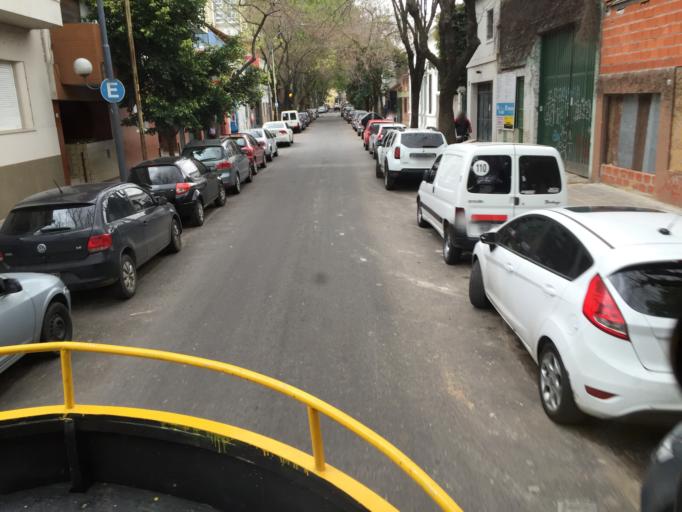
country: AR
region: Buenos Aires F.D.
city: Colegiales
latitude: -34.5542
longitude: -58.4482
